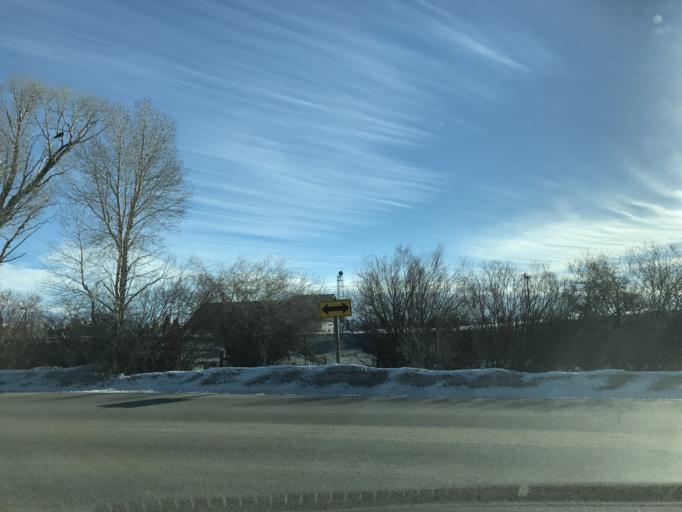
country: US
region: Wyoming
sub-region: Sublette County
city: Pinedale
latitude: 42.8521
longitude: -109.8613
